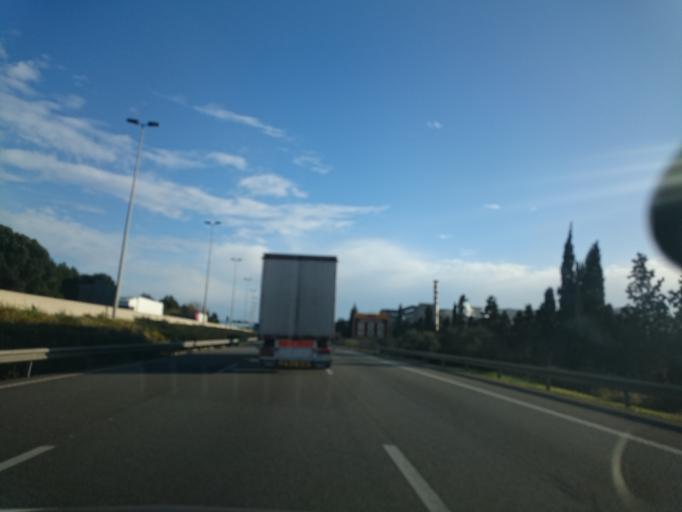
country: ES
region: Catalonia
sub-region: Provincia de Barcelona
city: Sant Andreu de la Barca
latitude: 41.4589
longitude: 1.9811
